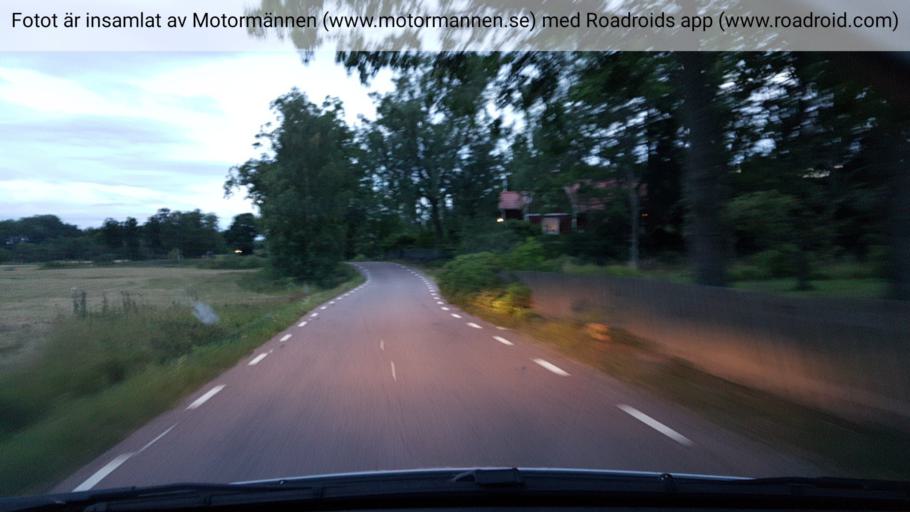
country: SE
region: Vaestmanland
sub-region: Vasteras
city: Tillberga
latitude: 59.5323
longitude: 16.7204
